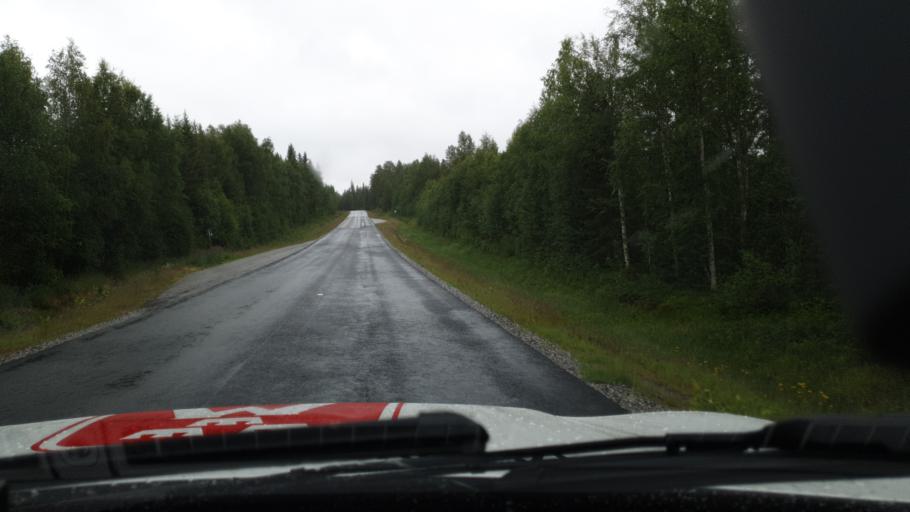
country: SE
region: Vaesterbotten
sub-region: Asele Kommun
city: Insjon
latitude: 64.2229
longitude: 17.5352
